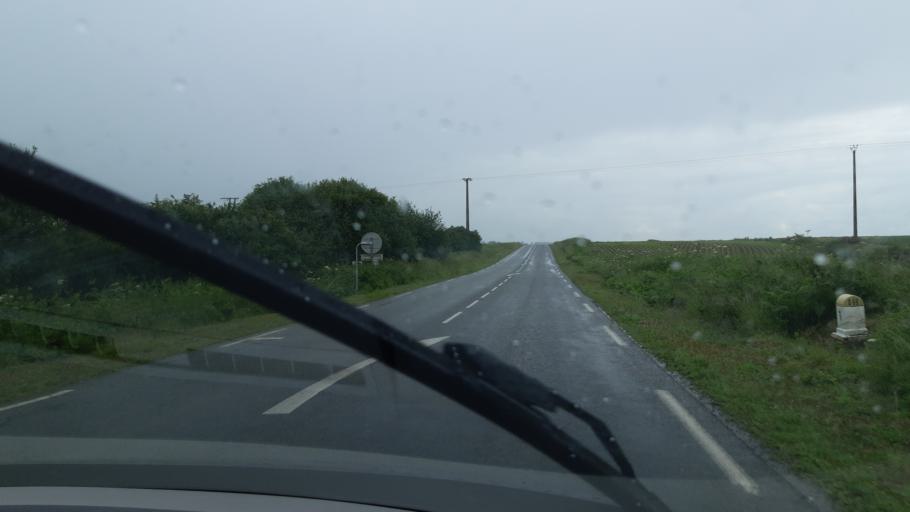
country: FR
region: Brittany
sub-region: Departement du Finistere
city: Plougoulm
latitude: 48.6423
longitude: -4.0502
